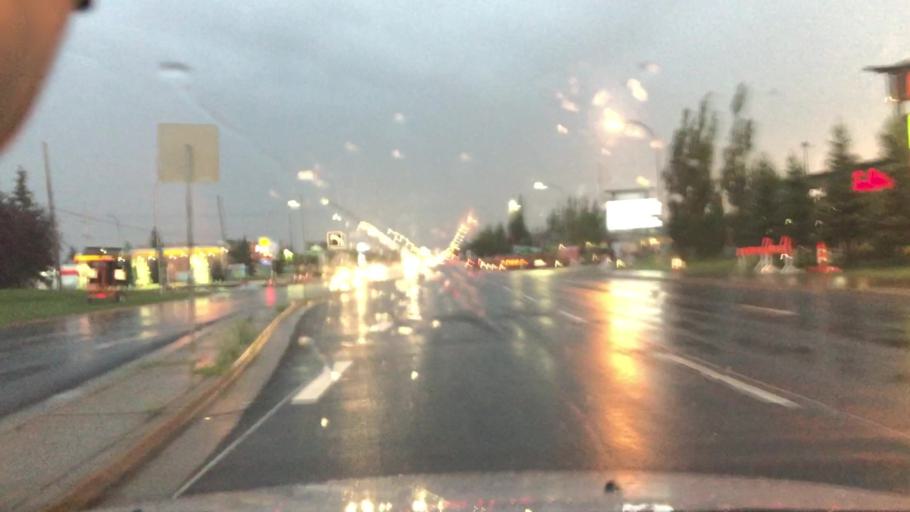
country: CA
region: Alberta
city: St. Albert
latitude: 53.6161
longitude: -113.5413
